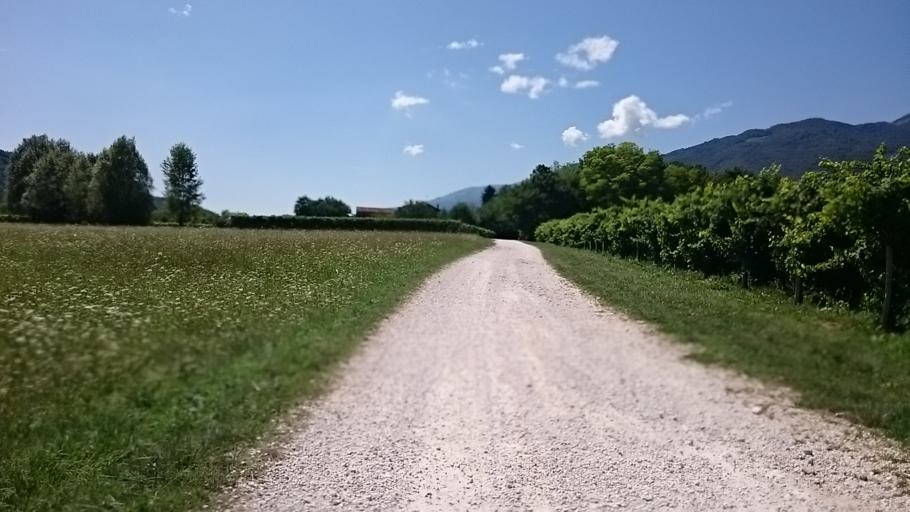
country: IT
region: Veneto
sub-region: Provincia di Treviso
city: Cison di Valmarino
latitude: 45.9631
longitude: 12.1522
